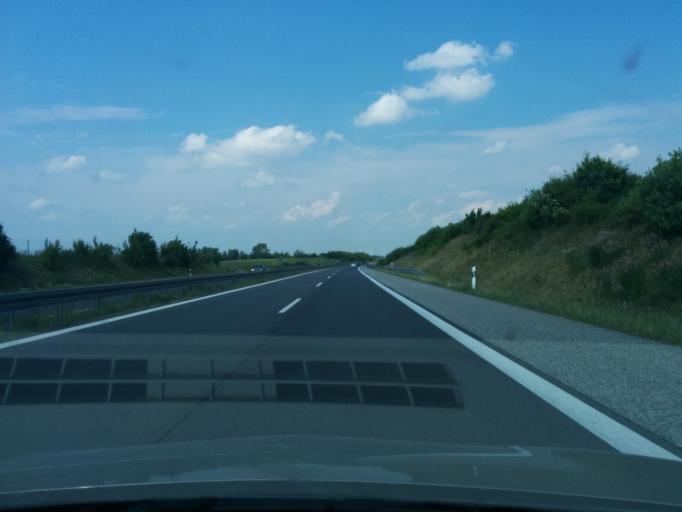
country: DE
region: Brandenburg
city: Grunow
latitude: 53.3233
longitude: 13.9909
